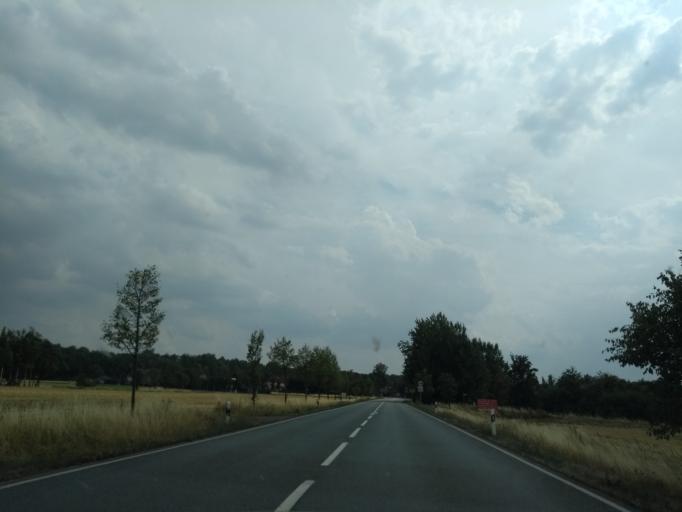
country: DE
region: Thuringia
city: Hirschfeld
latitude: 50.9716
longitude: 12.1352
